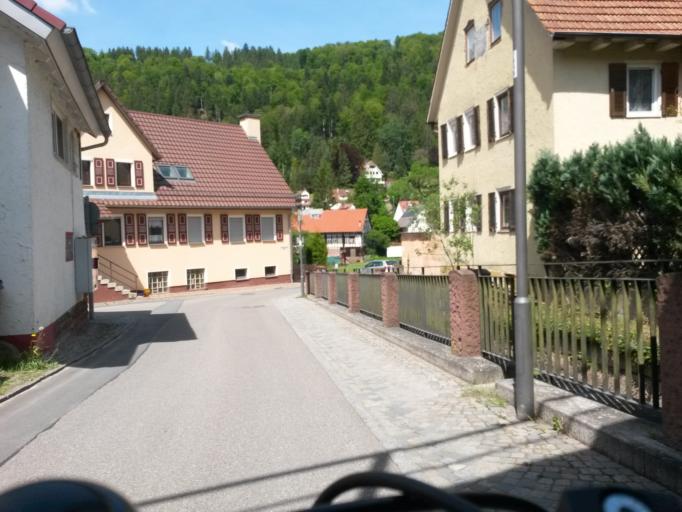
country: DE
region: Baden-Wuerttemberg
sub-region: Karlsruhe Region
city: Bad Liebenzell
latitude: 48.7487
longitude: 8.7331
